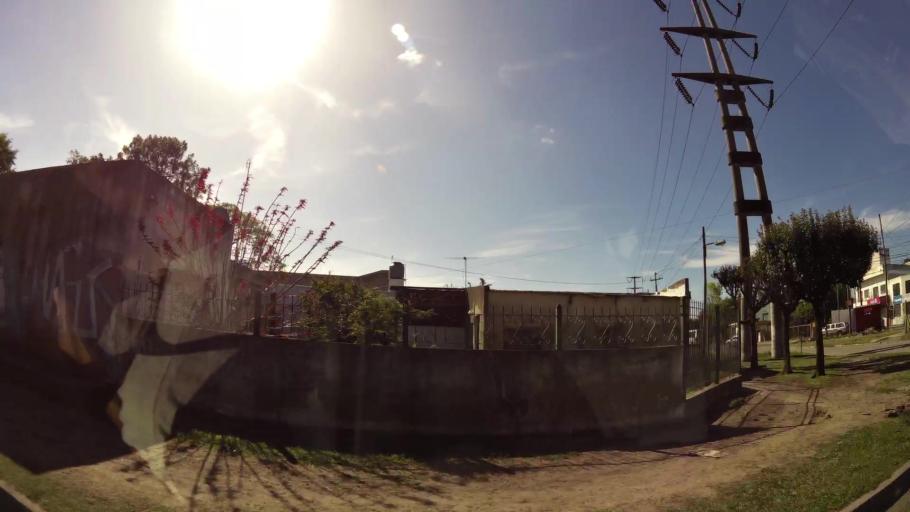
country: AR
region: Buenos Aires
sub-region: Partido de Quilmes
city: Quilmes
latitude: -34.8071
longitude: -58.2151
